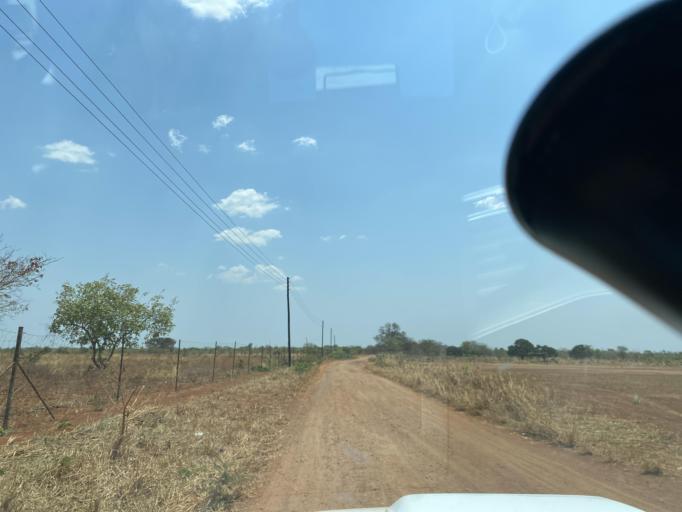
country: ZM
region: Lusaka
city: Lusaka
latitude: -15.5057
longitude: 28.0236
